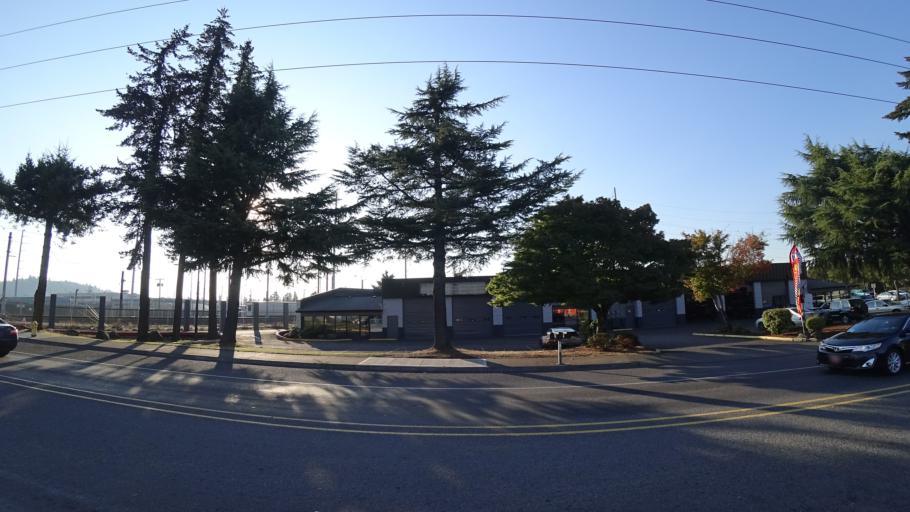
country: US
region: Oregon
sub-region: Multnomah County
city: Gresham
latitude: 45.5145
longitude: -122.4551
